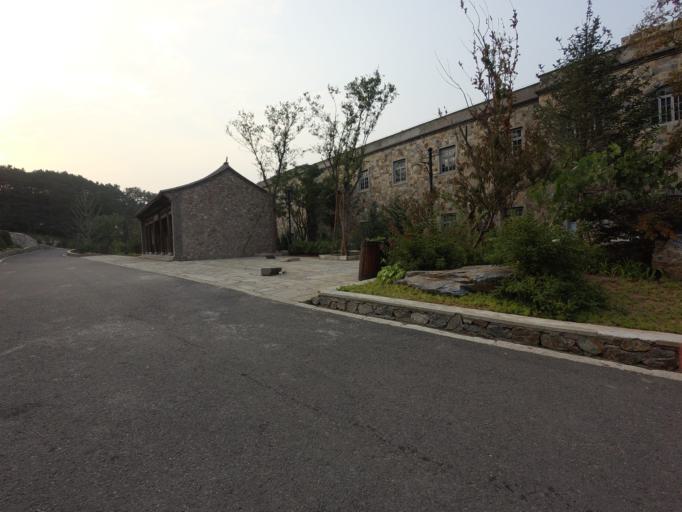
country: CN
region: Beijing
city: Xinchengzi
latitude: 40.6495
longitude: 117.2707
